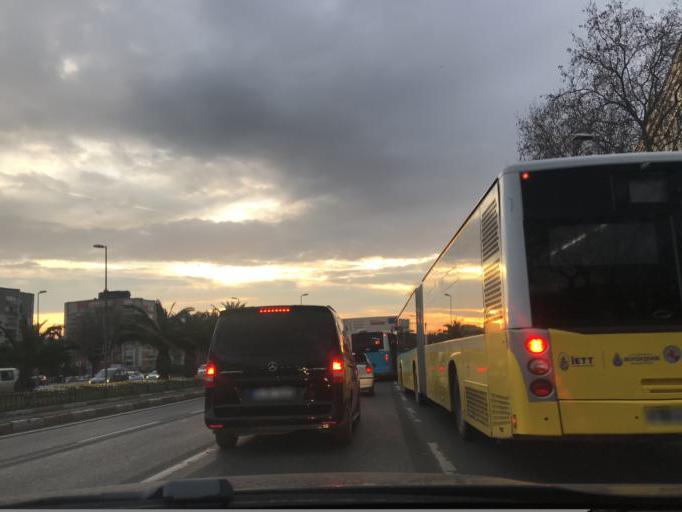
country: TR
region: Istanbul
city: Istanbul
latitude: 41.0238
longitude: 28.9302
